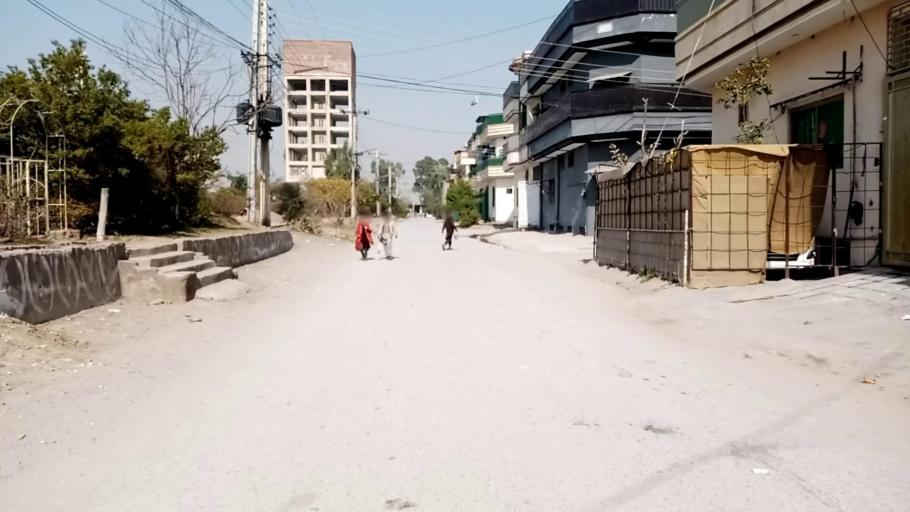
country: PK
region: Khyber Pakhtunkhwa
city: Peshawar
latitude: 33.9636
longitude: 71.4126
